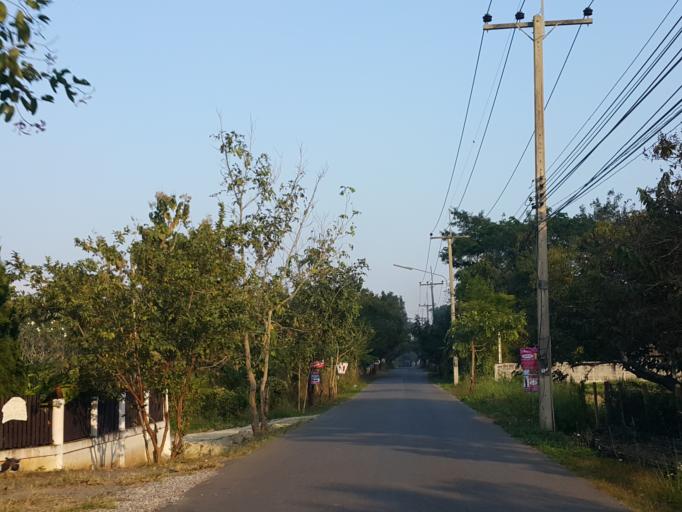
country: TH
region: Chiang Mai
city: Chiang Mai
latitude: 18.9085
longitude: 98.9090
